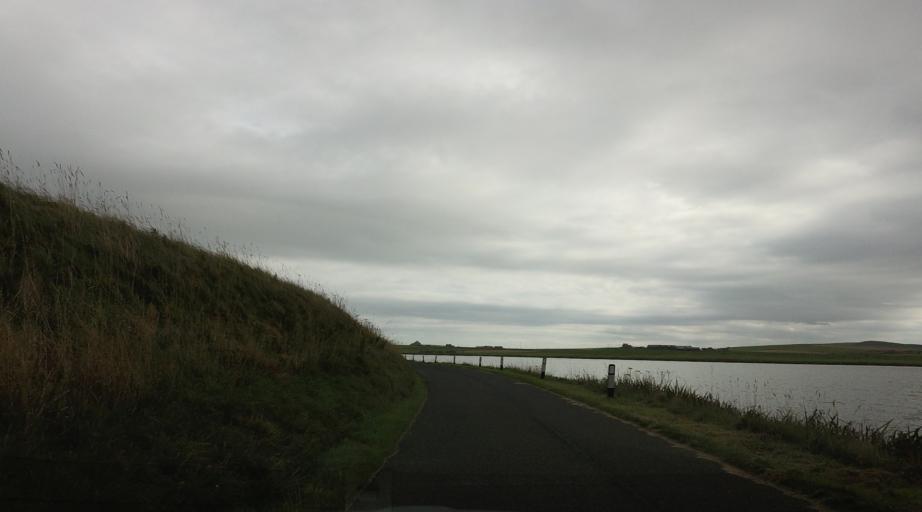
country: GB
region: Scotland
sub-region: Orkney Islands
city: Stromness
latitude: 59.0450
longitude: -3.3184
